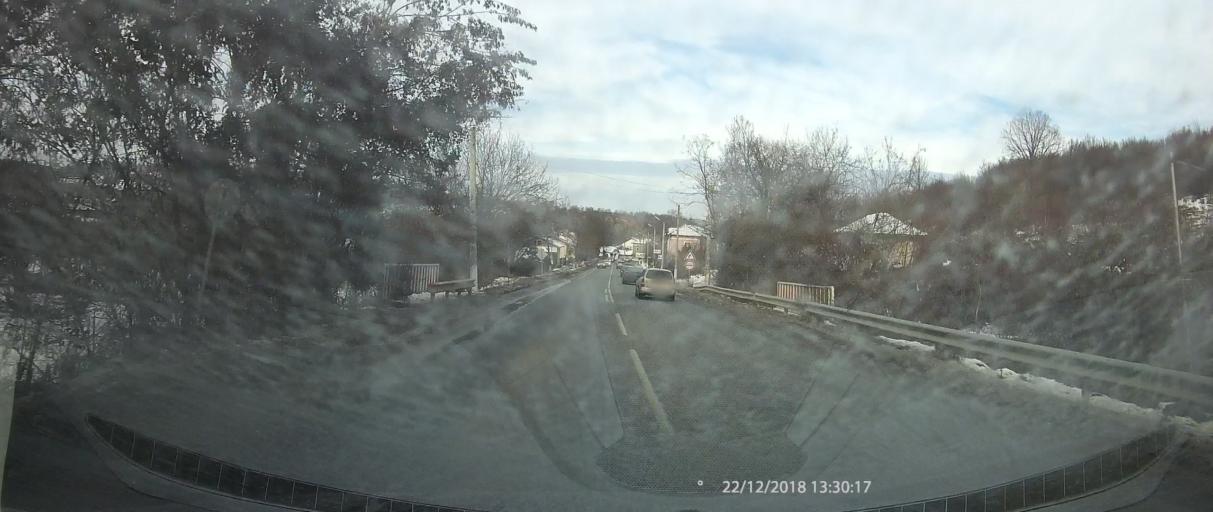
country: BG
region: Lovech
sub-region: Obshtina Yablanitsa
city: Yablanitsa
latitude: 43.0874
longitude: 24.1483
